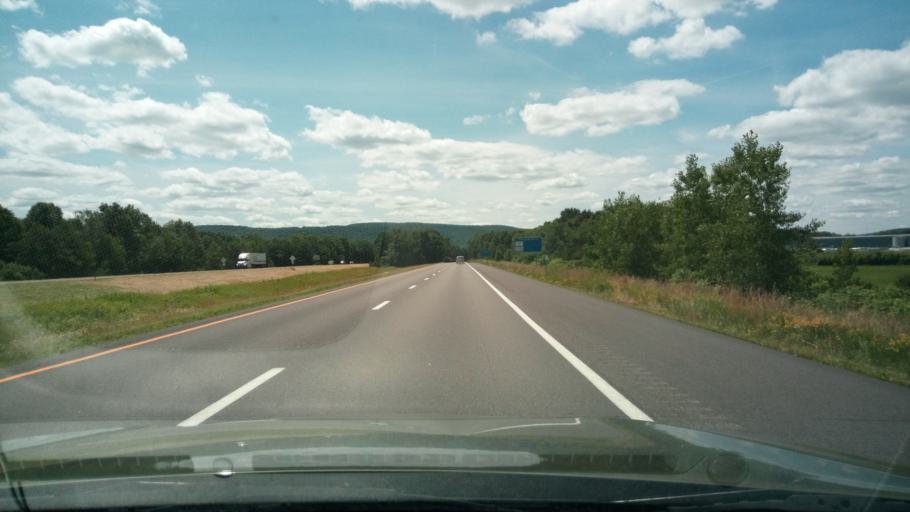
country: US
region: Pennsylvania
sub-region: Bradford County
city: South Waverly
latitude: 42.0014
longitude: -76.6091
